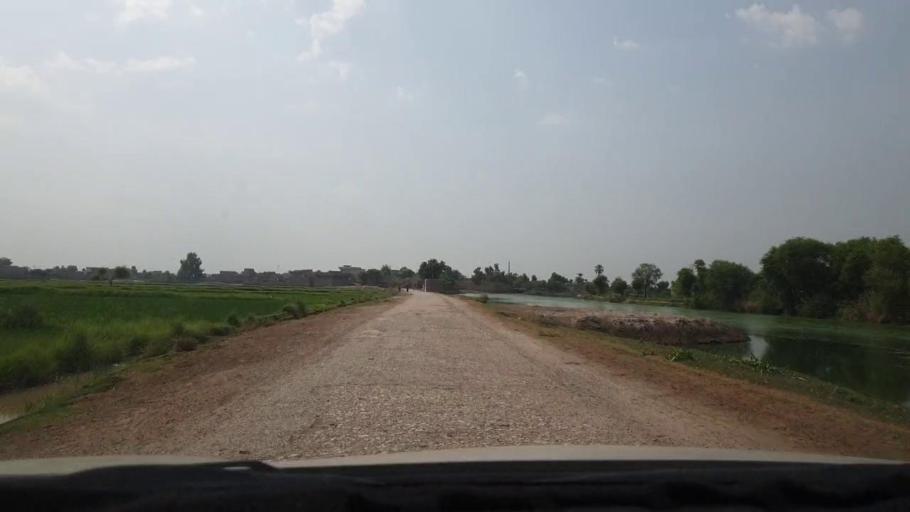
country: PK
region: Sindh
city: Dokri
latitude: 27.3823
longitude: 68.1255
